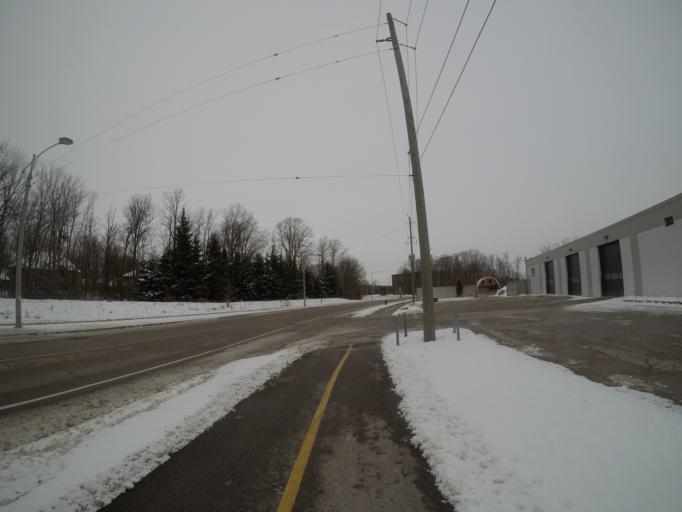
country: CA
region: Ontario
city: Waterloo
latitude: 43.4832
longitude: -80.5462
